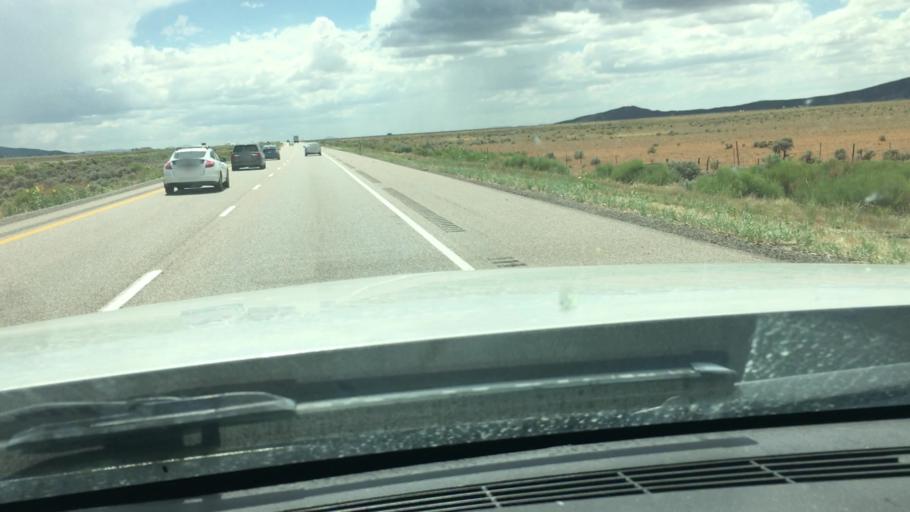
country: US
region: Utah
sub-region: Iron County
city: Parowan
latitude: 37.8288
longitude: -112.8982
